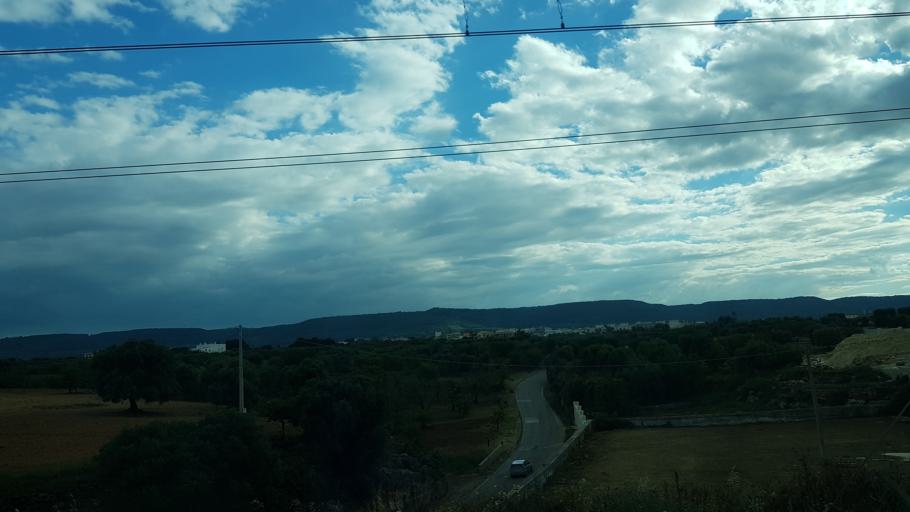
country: IT
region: Apulia
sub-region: Provincia di Brindisi
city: Montalbano
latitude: 40.8152
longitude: 17.4596
